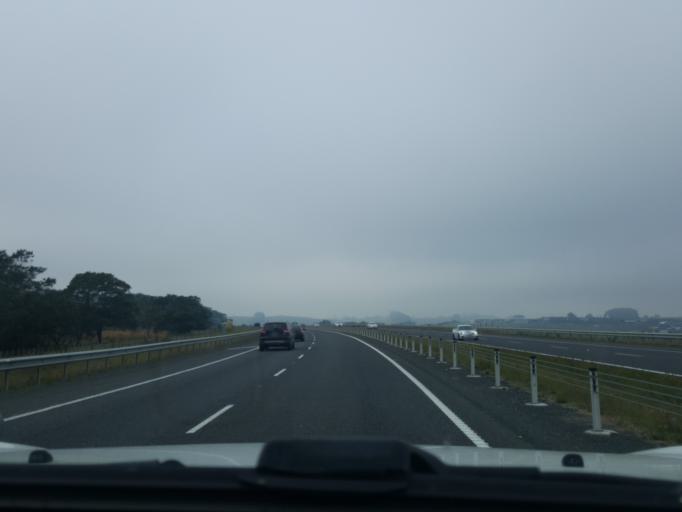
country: NZ
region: Waikato
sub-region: Waikato District
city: Te Kauwhata
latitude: -37.3455
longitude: 175.0699
